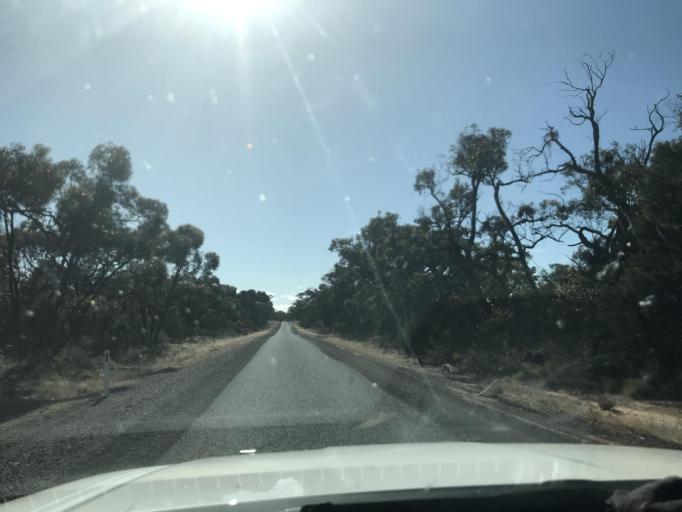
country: AU
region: Victoria
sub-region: Horsham
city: Horsham
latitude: -37.0233
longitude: 141.6869
